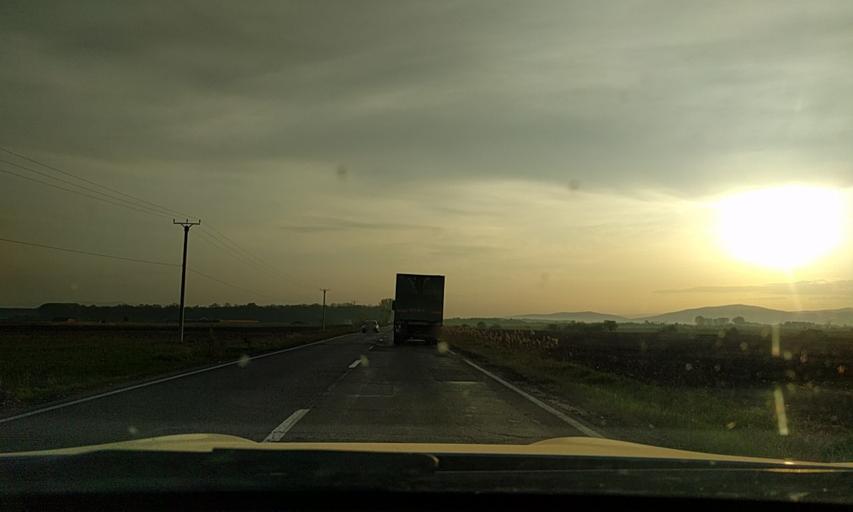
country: RO
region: Brasov
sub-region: Comuna Prejmer
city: Prejmer
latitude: 45.7234
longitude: 25.7266
